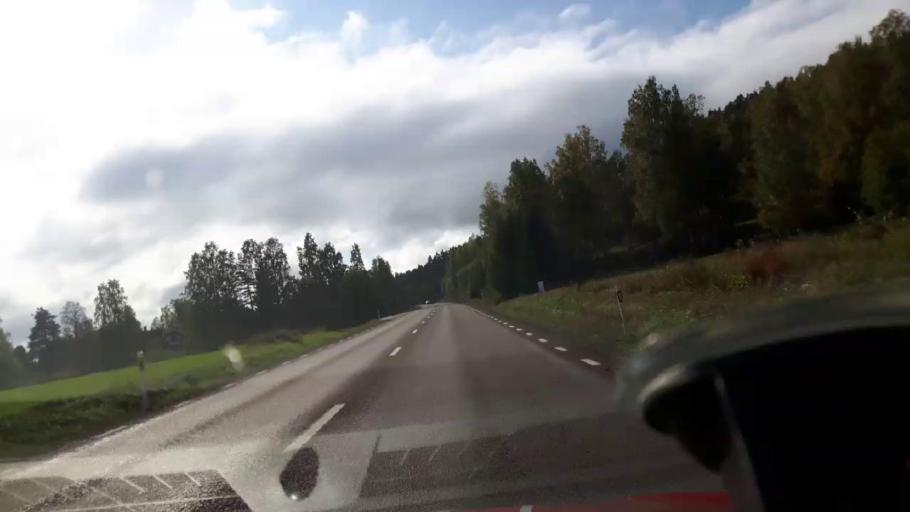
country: SE
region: Gaevleborg
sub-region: Ljusdals Kommun
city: Jaervsoe
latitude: 61.7461
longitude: 16.1592
